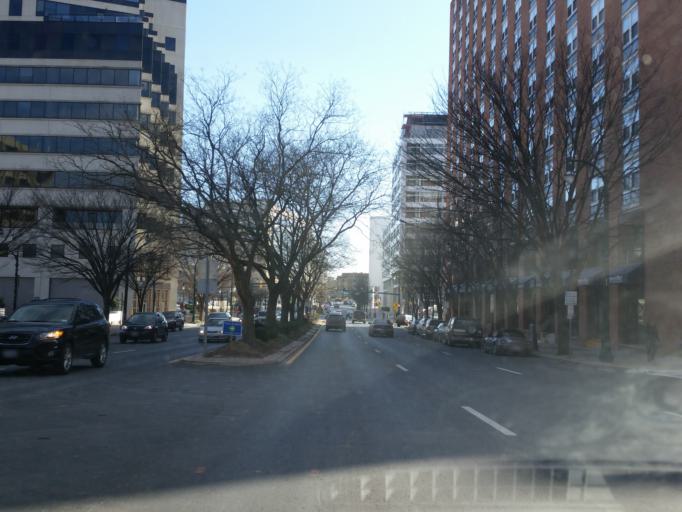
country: US
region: Maryland
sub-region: Montgomery County
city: Silver Spring
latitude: 38.9971
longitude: -77.0292
